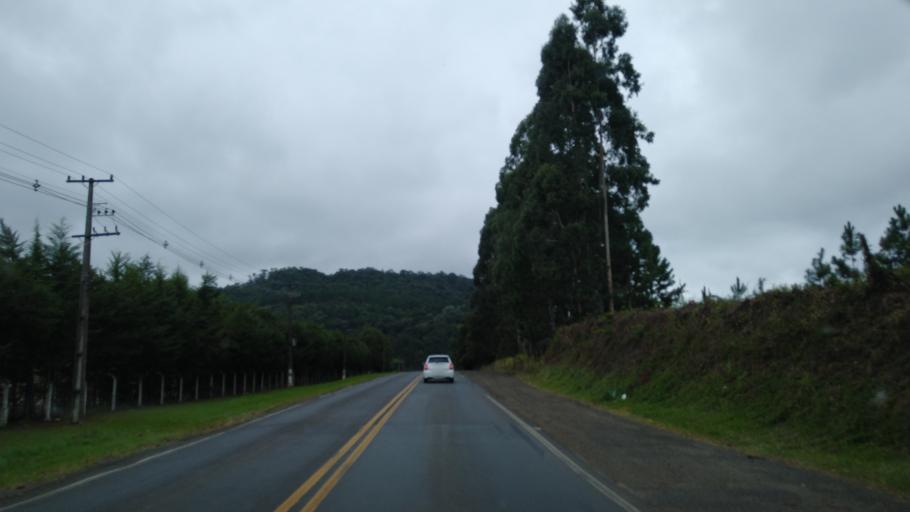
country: BR
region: Parana
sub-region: Uniao Da Vitoria
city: Uniao da Vitoria
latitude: -26.2340
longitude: -51.1263
